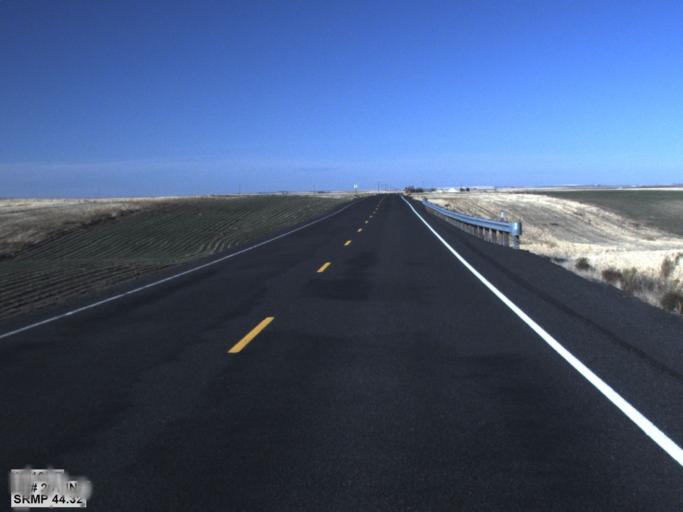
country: US
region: Washington
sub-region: Adams County
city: Ritzville
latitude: 46.8613
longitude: -118.3360
